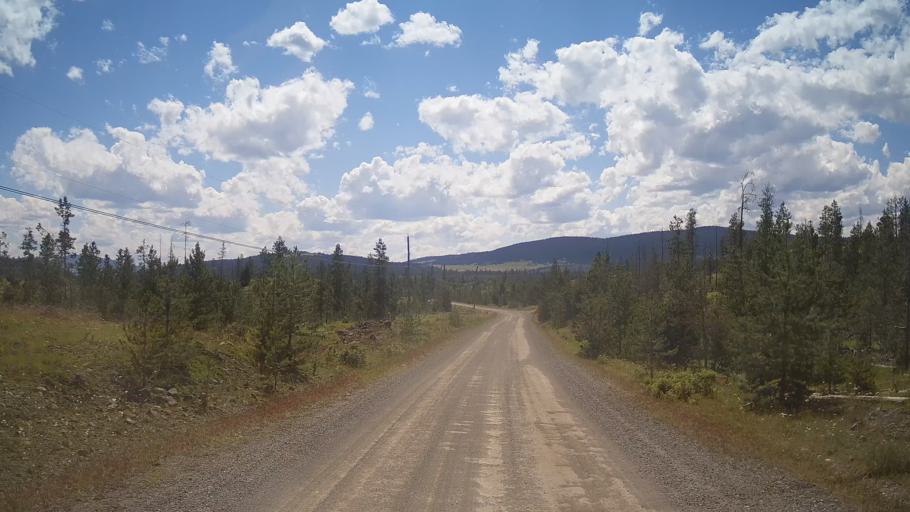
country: CA
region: British Columbia
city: Lillooet
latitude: 51.3343
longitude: -121.9729
